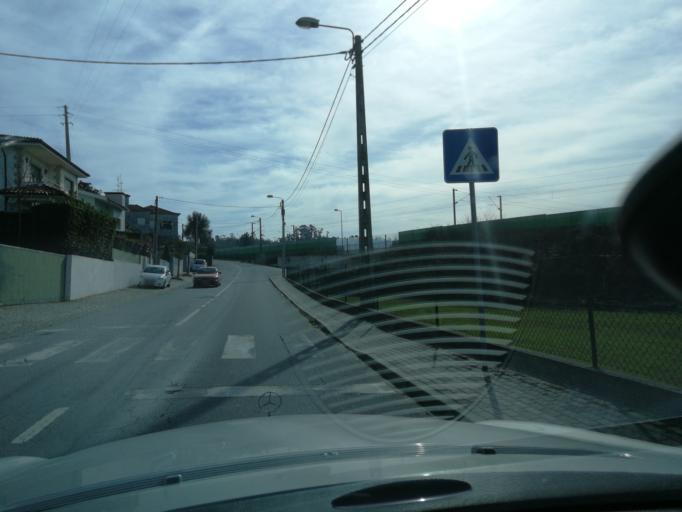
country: PT
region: Braga
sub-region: Vila Nova de Famalicao
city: Vila Nova de Famalicao
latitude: 41.4317
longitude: -8.5224
